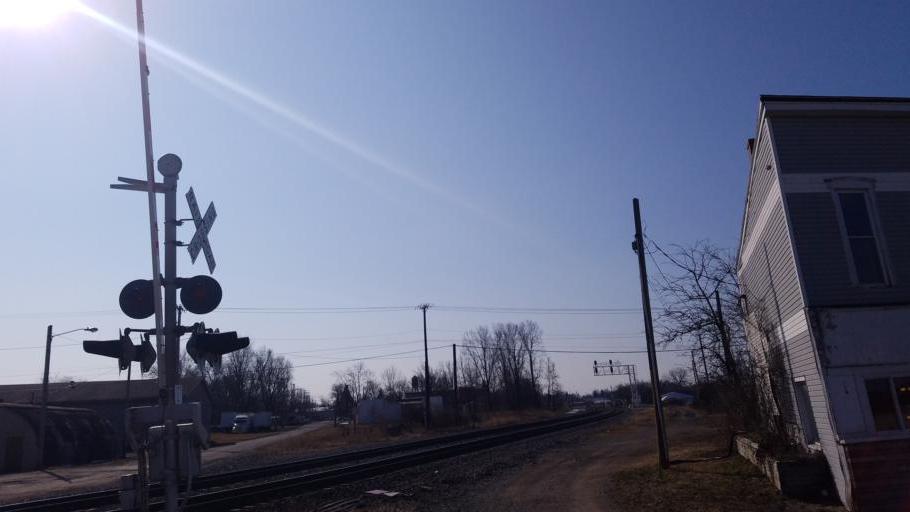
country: US
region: Ohio
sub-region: Crawford County
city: Galion
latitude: 40.7338
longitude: -82.7843
